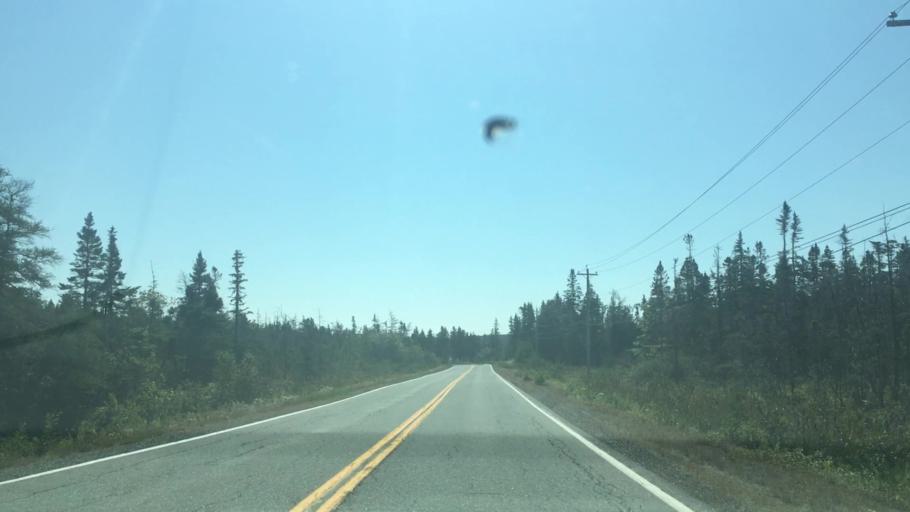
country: CA
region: Nova Scotia
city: Antigonish
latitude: 45.0100
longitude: -62.0907
